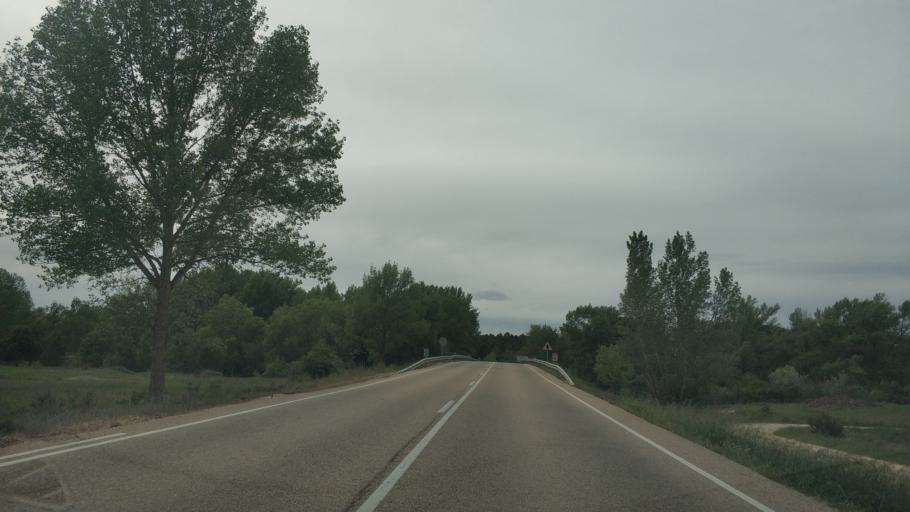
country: ES
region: Castille and Leon
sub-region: Provincia de Soria
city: Bayubas de Abajo
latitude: 41.5017
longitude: -2.8873
